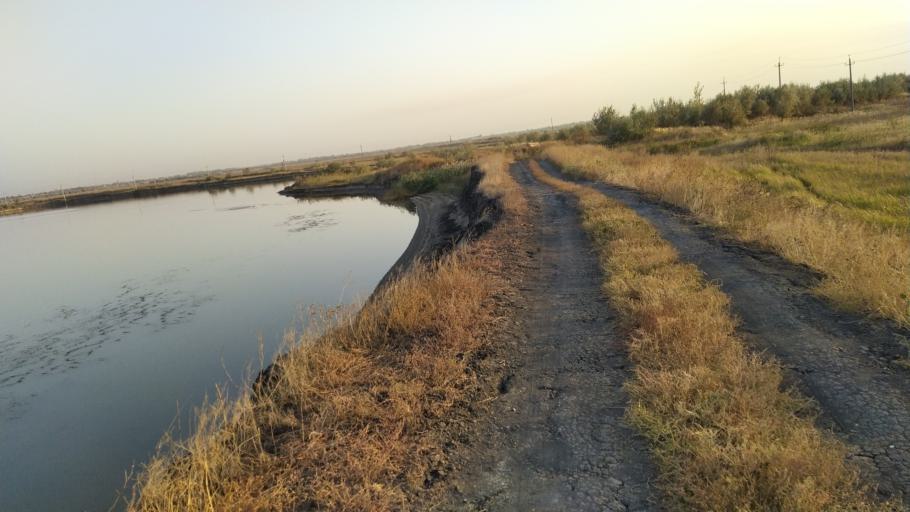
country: RU
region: Rostov
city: Kuleshovka
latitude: 47.1409
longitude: 39.6446
